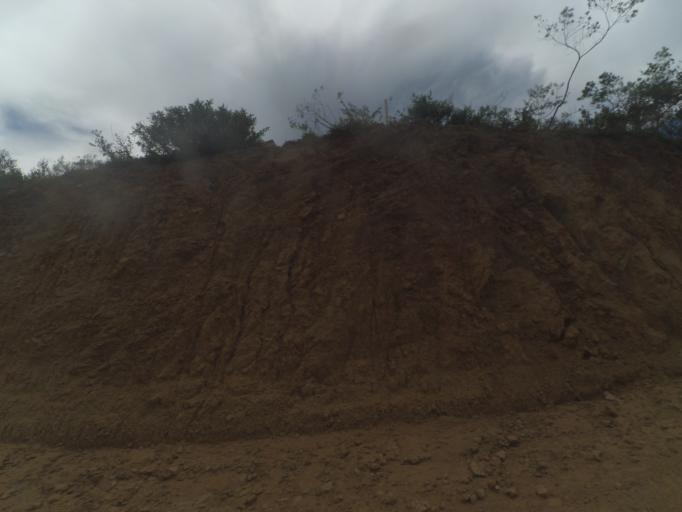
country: BO
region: Chuquisaca
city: Padilla
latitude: -19.3476
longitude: -64.2908
